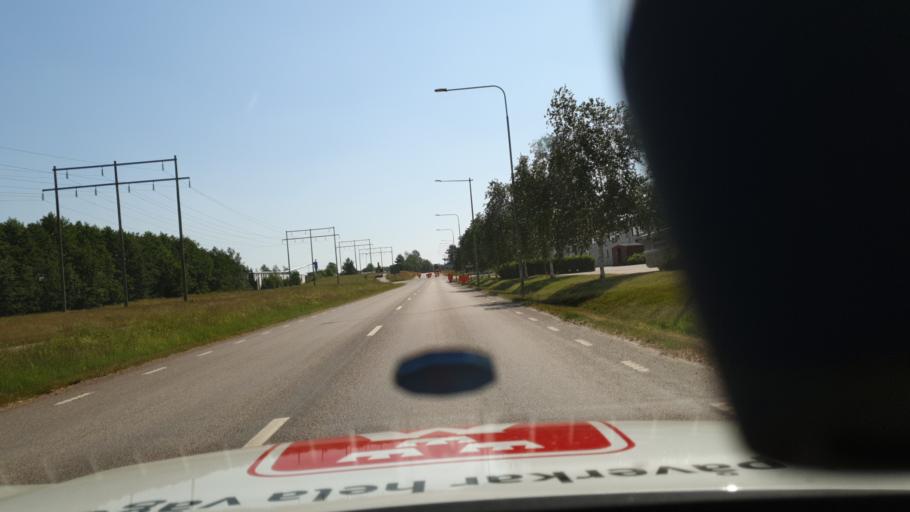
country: SE
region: Vaestra Goetaland
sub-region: Tibro Kommun
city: Tibro
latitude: 58.4144
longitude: 14.1453
